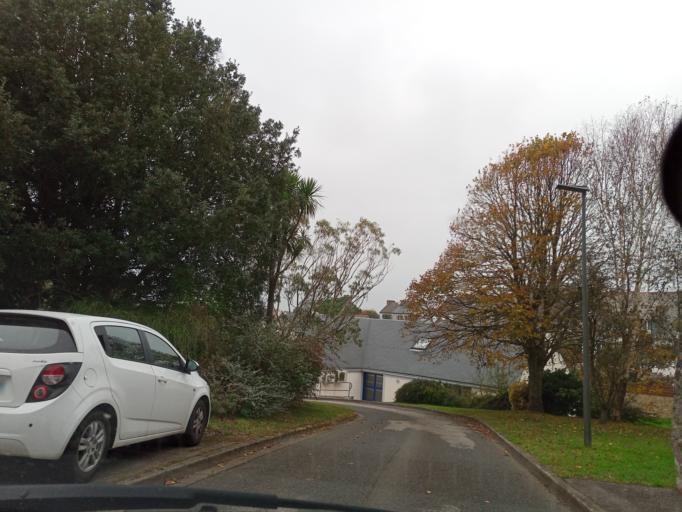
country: FR
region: Brittany
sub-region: Departement du Finistere
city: Esquibien
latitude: 48.0251
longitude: -4.5623
